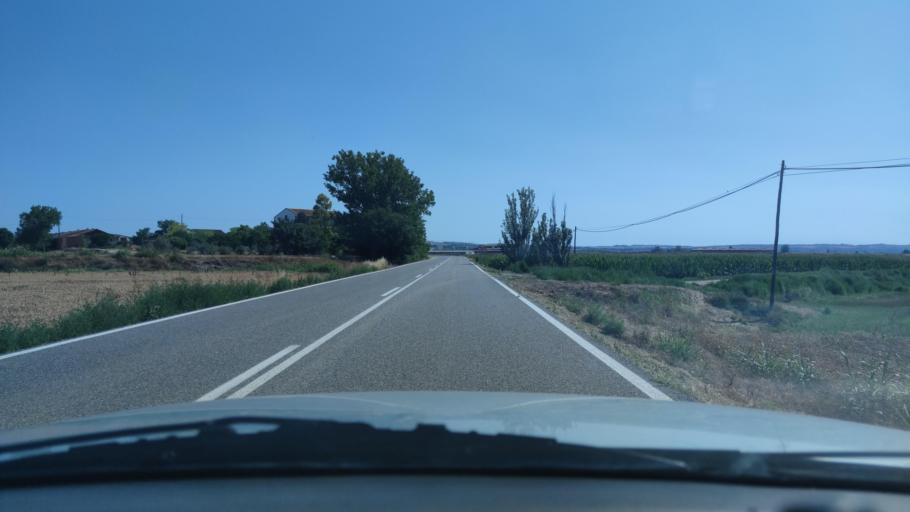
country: ES
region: Catalonia
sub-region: Provincia de Lleida
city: Penelles
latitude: 41.7388
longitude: 0.9461
